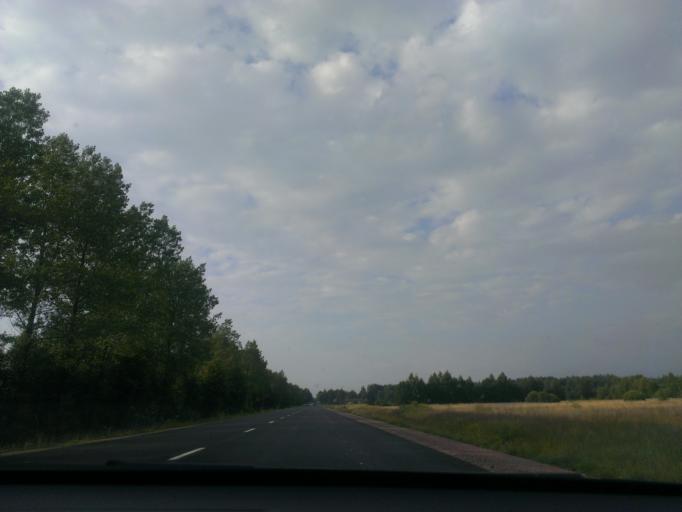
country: LV
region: Lecava
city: Iecava
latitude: 56.6858
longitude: 24.2396
